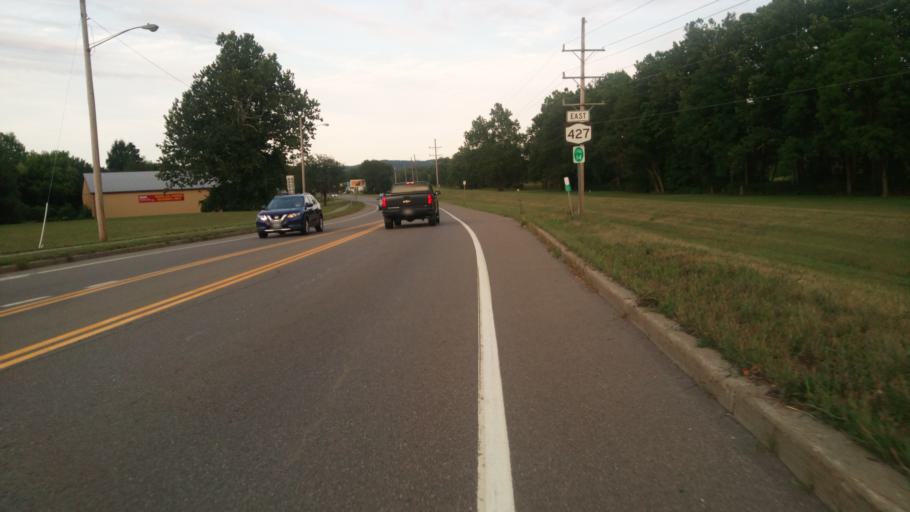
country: US
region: New York
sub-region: Chemung County
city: Southport
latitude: 42.0578
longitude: -76.8051
